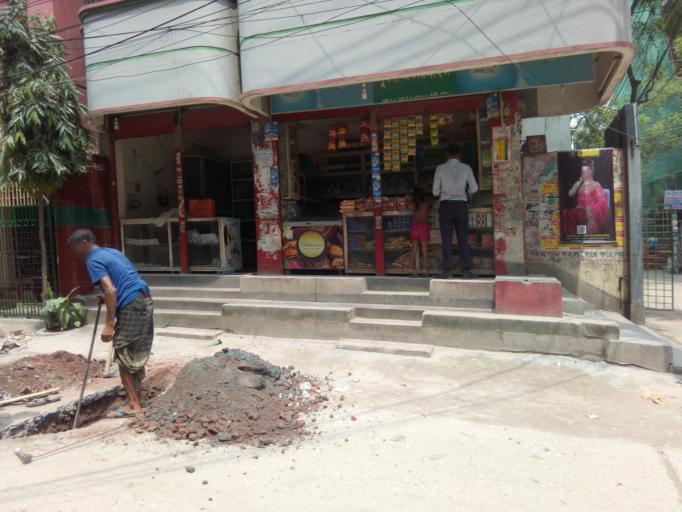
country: BD
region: Dhaka
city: Paltan
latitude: 23.7653
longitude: 90.4252
